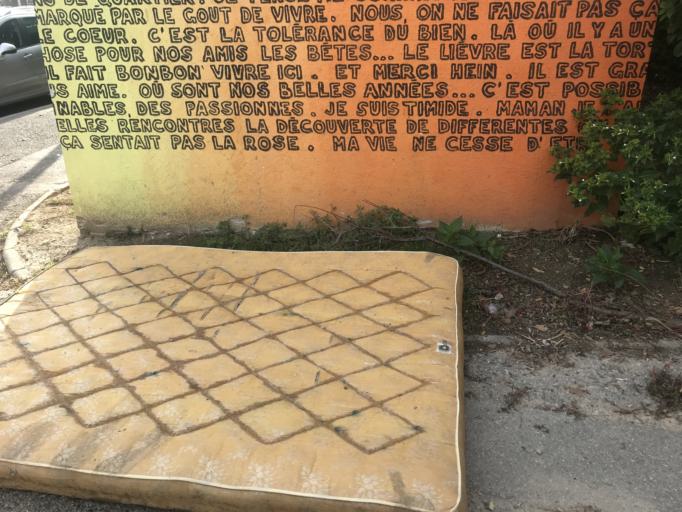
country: FR
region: Provence-Alpes-Cote d'Azur
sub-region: Departement des Bouches-du-Rhone
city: Aix-en-Provence
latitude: 43.5197
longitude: 5.4321
